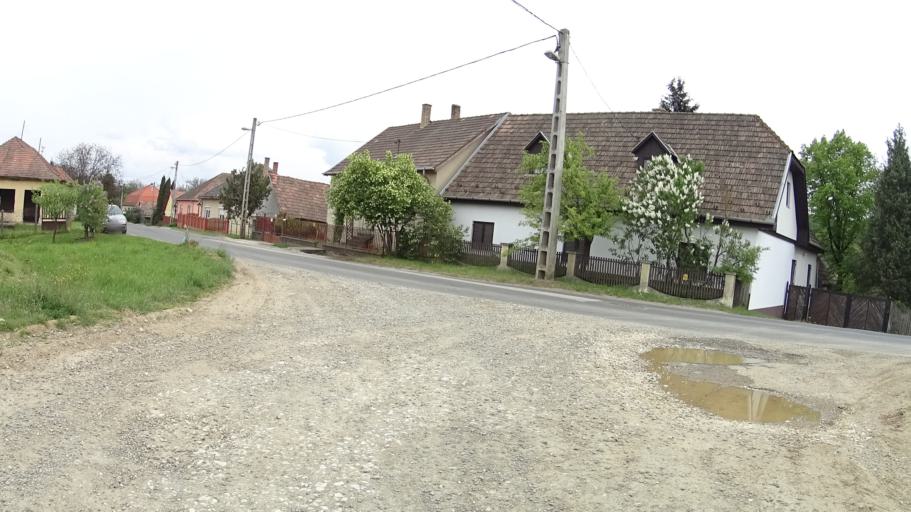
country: HU
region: Pest
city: Acsa
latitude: 47.8100
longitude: 19.3225
